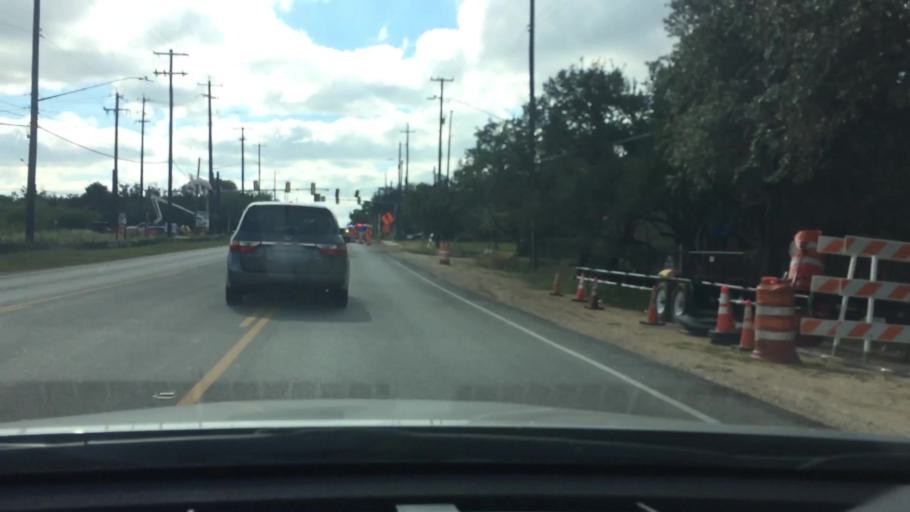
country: US
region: Texas
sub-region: Bexar County
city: Shavano Park
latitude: 29.5754
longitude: -98.5671
